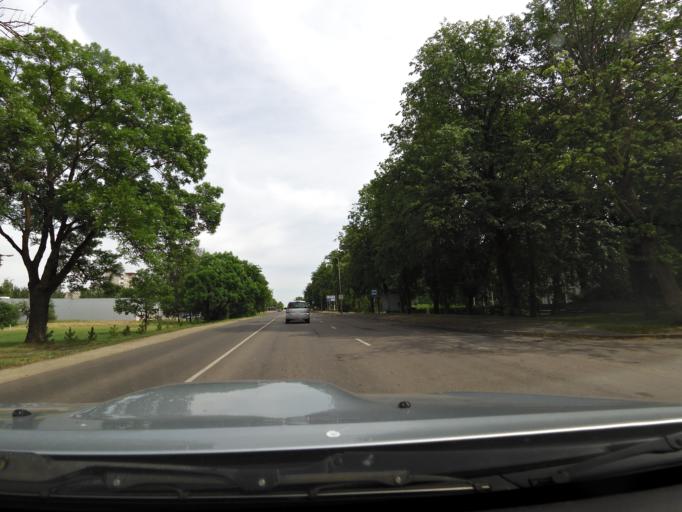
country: LT
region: Marijampoles apskritis
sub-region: Marijampole Municipality
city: Marijampole
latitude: 54.5645
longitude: 23.3268
